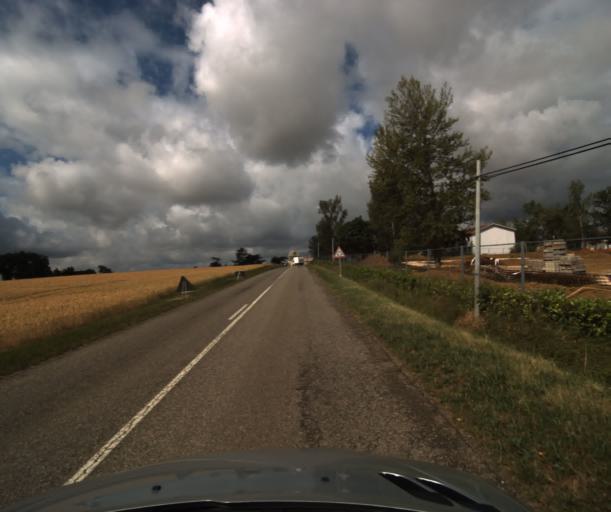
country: FR
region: Midi-Pyrenees
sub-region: Departement du Tarn-et-Garonne
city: Lavit
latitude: 43.9669
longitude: 0.9379
